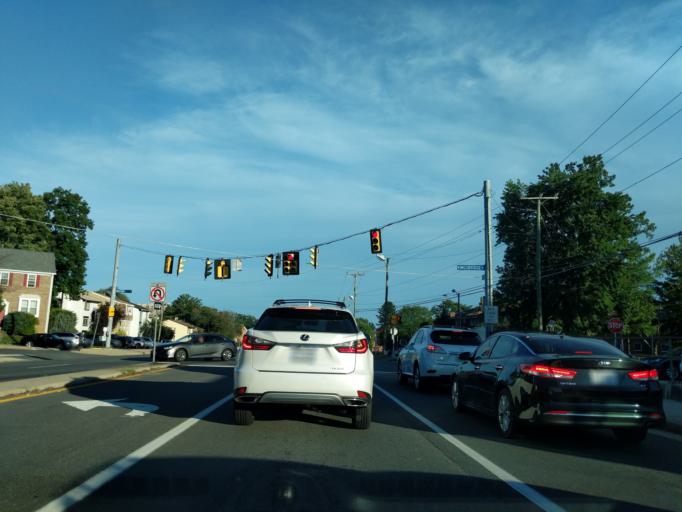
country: US
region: Virginia
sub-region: Fairfax County
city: Mantua
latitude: 38.8693
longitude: -77.2775
